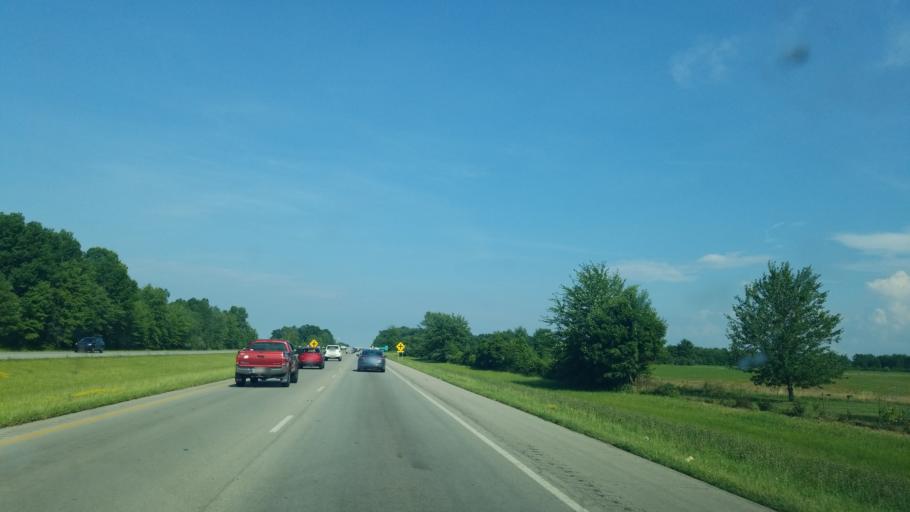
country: US
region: Ohio
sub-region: Clermont County
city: Batavia
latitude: 39.0806
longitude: -84.1402
